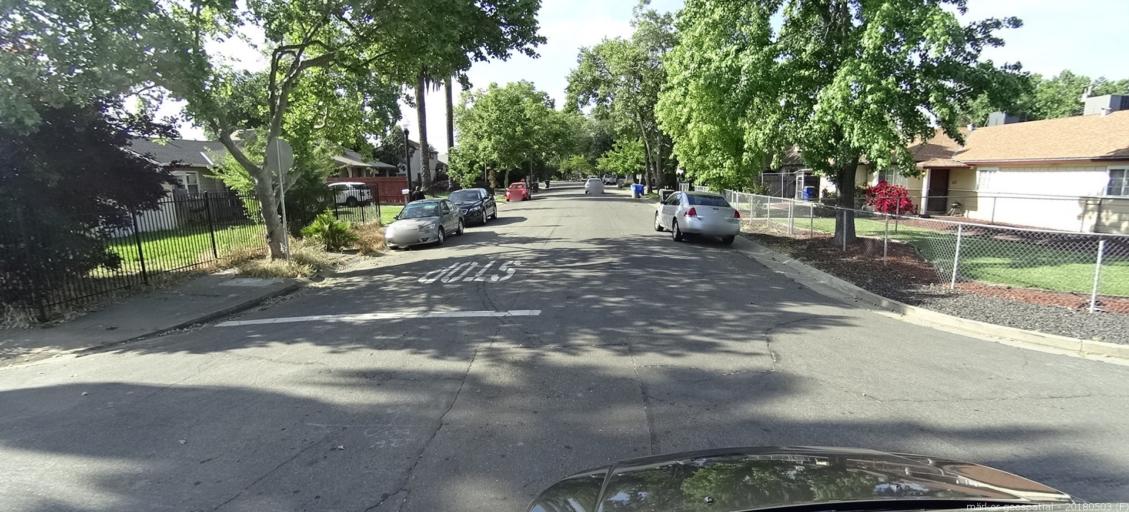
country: US
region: California
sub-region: Sacramento County
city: Sacramento
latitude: 38.6075
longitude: -121.4508
